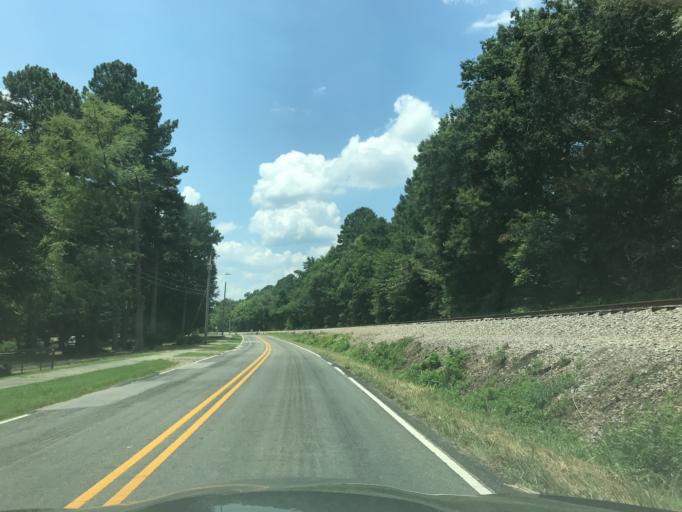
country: US
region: North Carolina
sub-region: Wake County
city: Wake Forest
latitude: 35.9859
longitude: -78.5042
